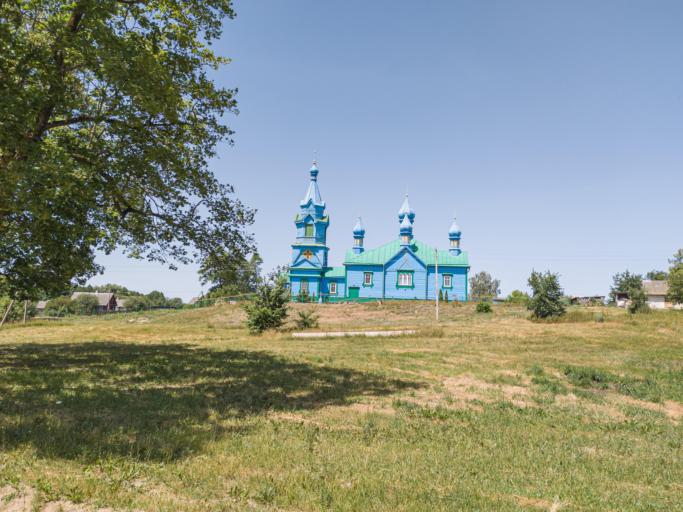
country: BY
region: Brest
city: Kamyanyets
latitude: 52.3940
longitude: 23.7643
